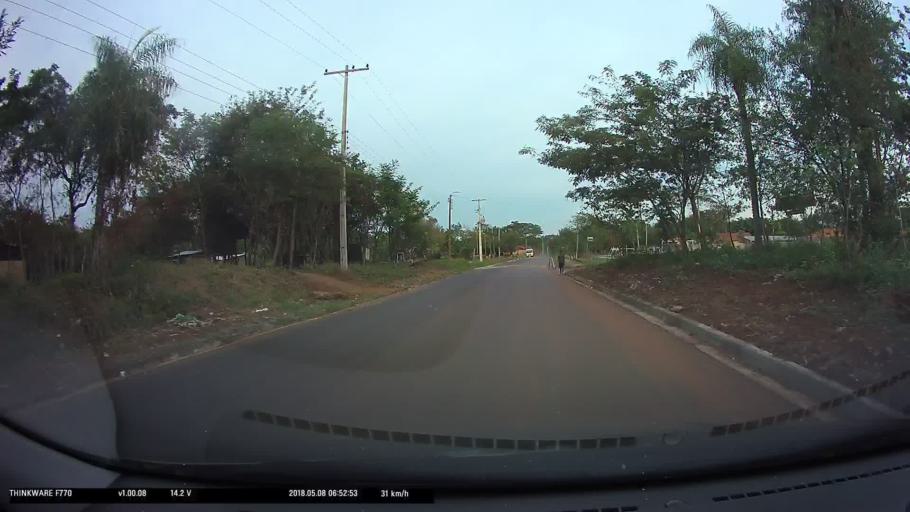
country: PY
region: Central
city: Limpio
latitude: -25.2345
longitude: -57.4678
